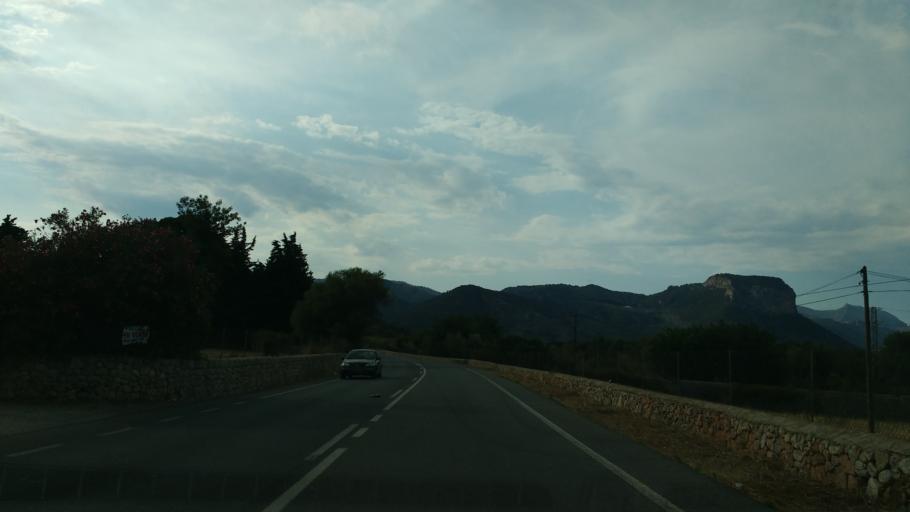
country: ES
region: Balearic Islands
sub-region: Illes Balears
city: Alaro
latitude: 39.6892
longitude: 2.8062
